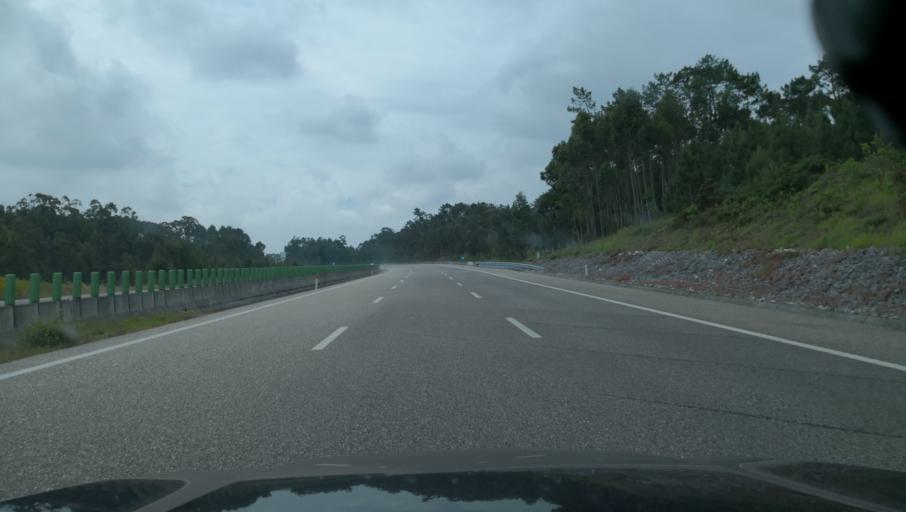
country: PT
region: Leiria
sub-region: Pombal
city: Lourical
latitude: 39.9746
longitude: -8.7826
